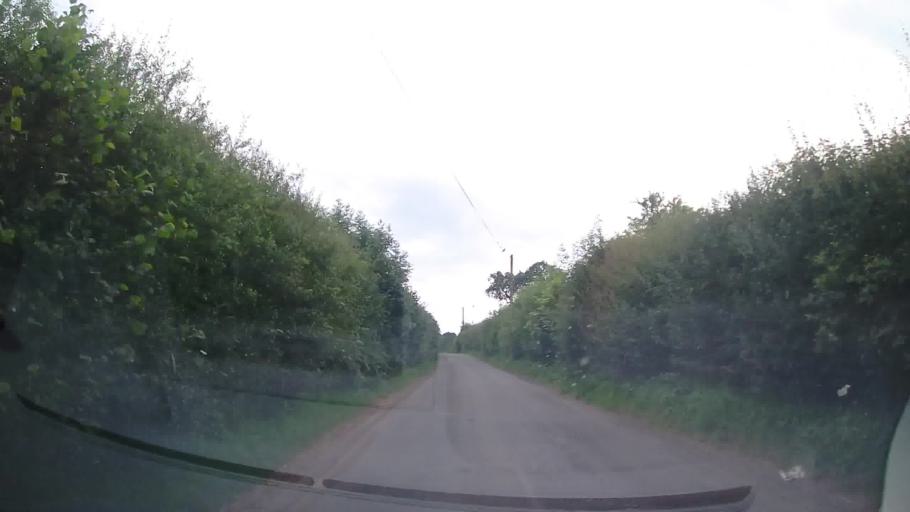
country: GB
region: England
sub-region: Shropshire
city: Whitchurch
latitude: 52.9332
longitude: -2.7245
